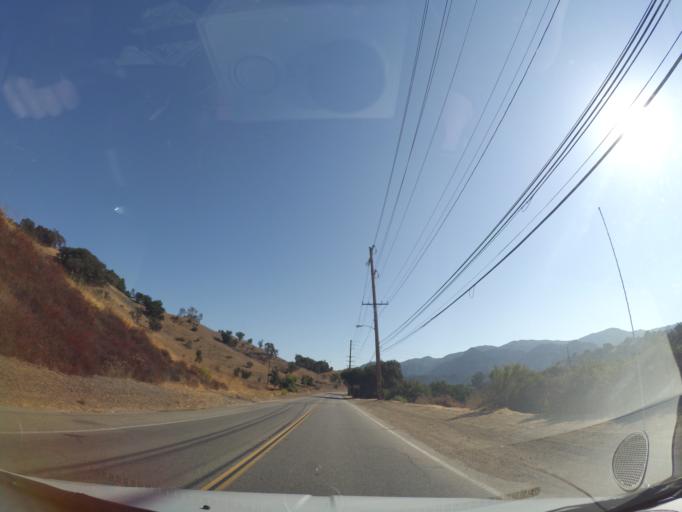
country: US
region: California
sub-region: Los Angeles County
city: Agoura
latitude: 34.1085
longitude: -118.7115
